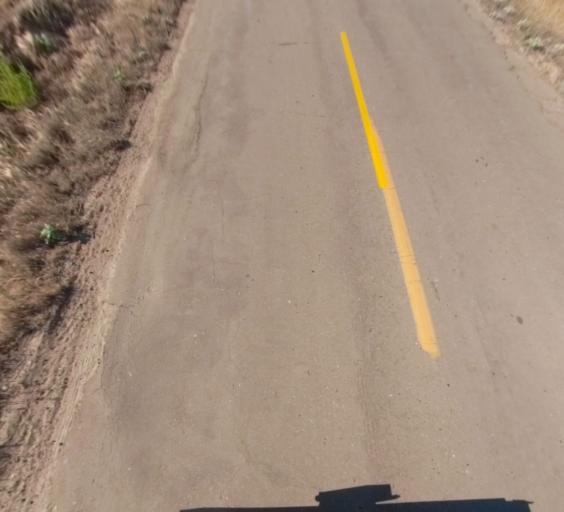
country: US
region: California
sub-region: Madera County
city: Bonadelle Ranchos-Madera Ranchos
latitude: 36.8861
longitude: -119.8110
